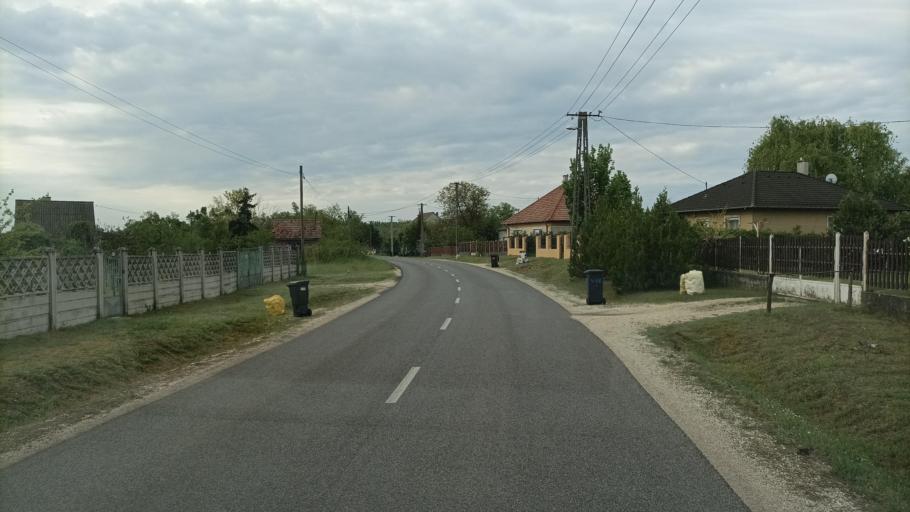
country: HU
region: Pest
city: Monor
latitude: 47.3175
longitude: 19.4116
